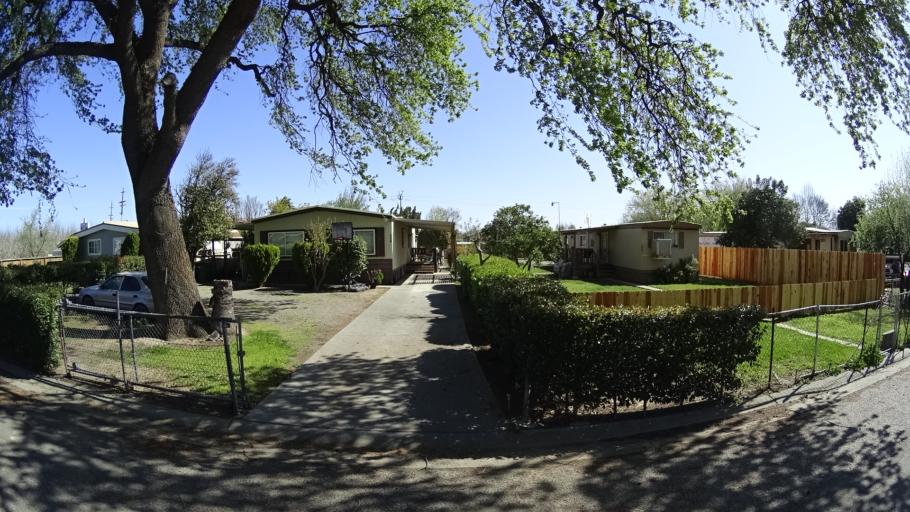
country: US
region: California
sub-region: Glenn County
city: Hamilton City
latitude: 39.7462
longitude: -122.0103
